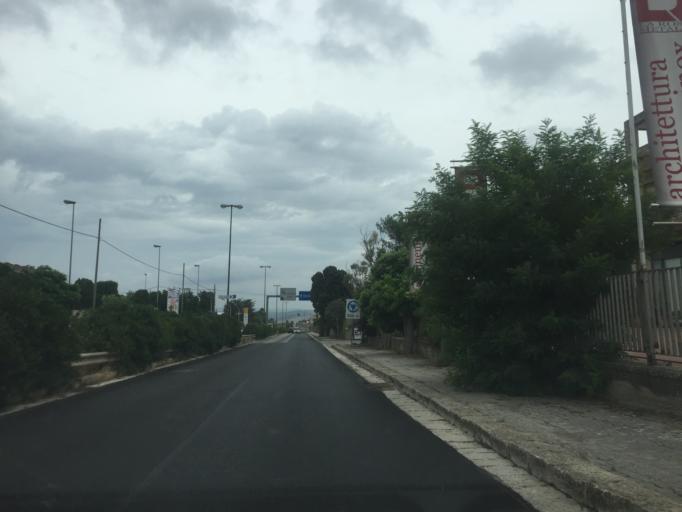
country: IT
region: Sicily
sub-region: Ragusa
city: Ragusa
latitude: 36.9037
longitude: 14.7178
